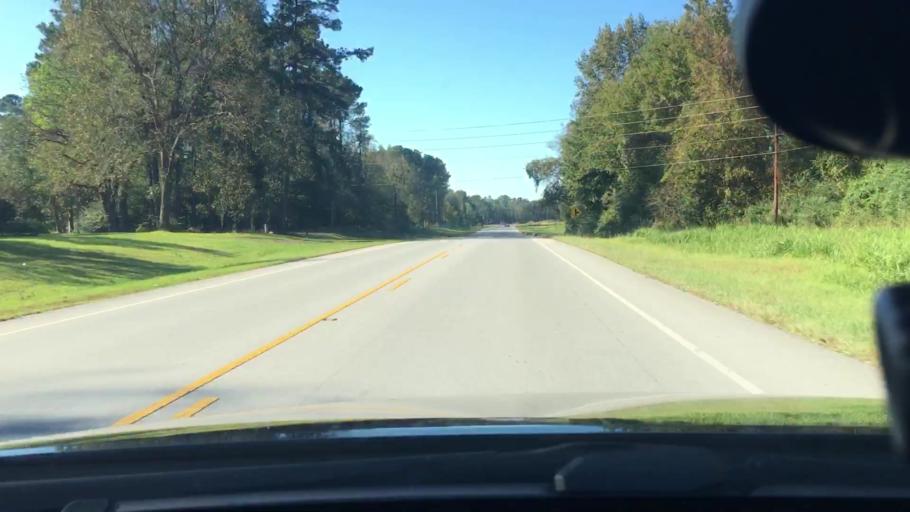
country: US
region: North Carolina
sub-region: Craven County
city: Trent Woods
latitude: 35.1690
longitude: -77.1252
